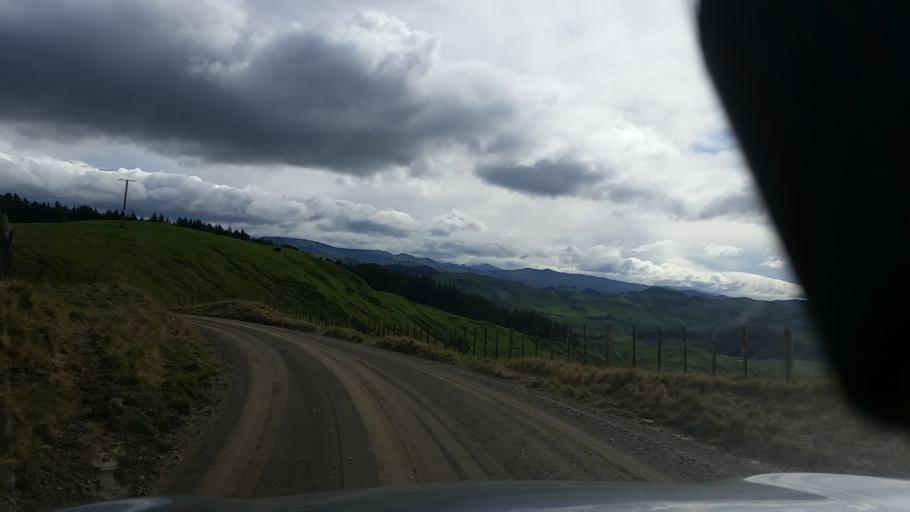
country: NZ
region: Hawke's Bay
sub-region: Napier City
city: Napier
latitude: -39.2069
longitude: 176.9337
